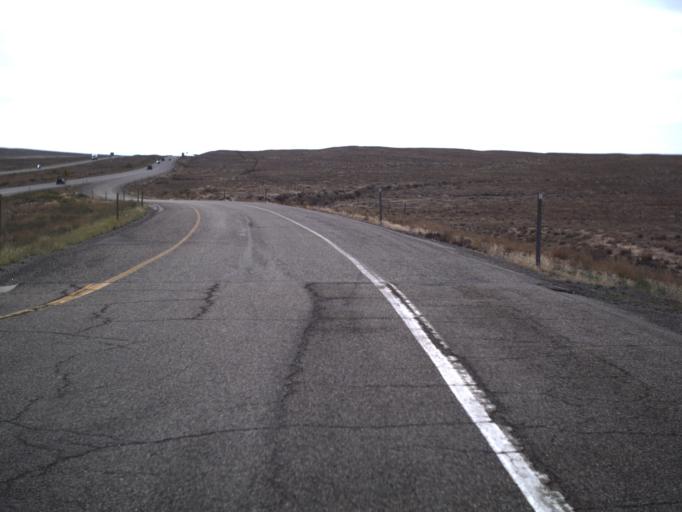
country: US
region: Colorado
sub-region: Mesa County
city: Loma
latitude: 39.1141
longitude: -109.1847
